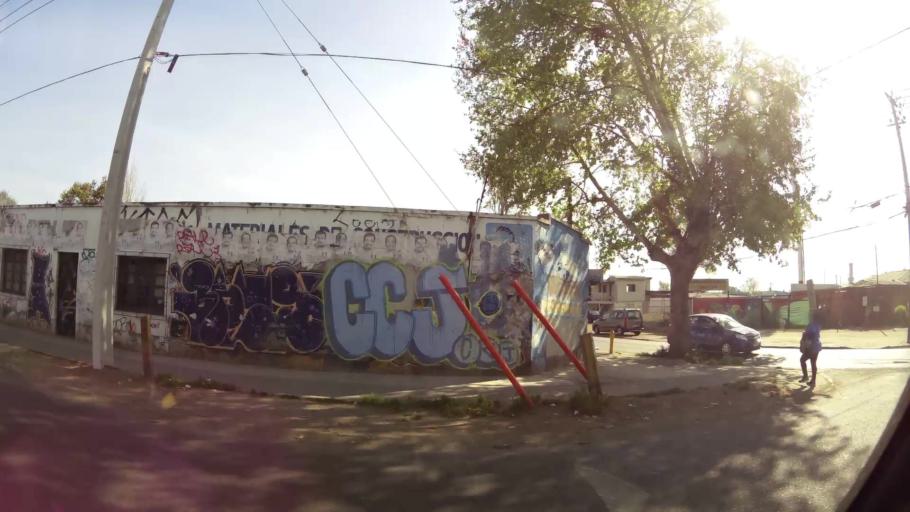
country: CL
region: Santiago Metropolitan
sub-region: Provincia de Santiago
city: Lo Prado
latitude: -33.4149
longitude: -70.7424
